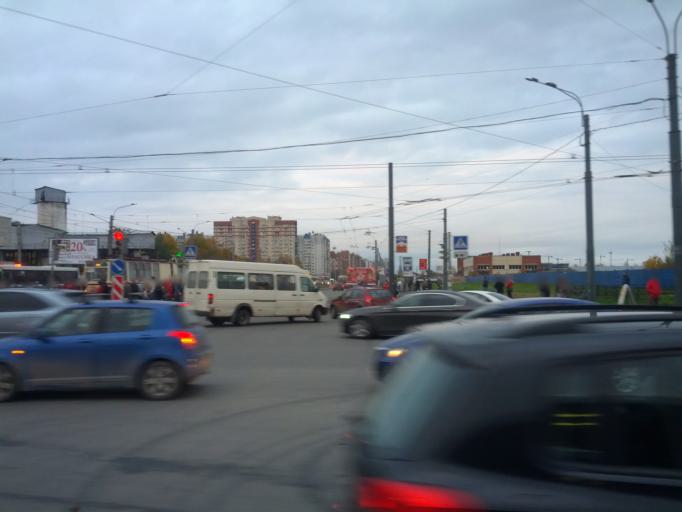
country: RU
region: St.-Petersburg
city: Krasnogvargeisky
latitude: 59.9067
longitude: 30.4827
